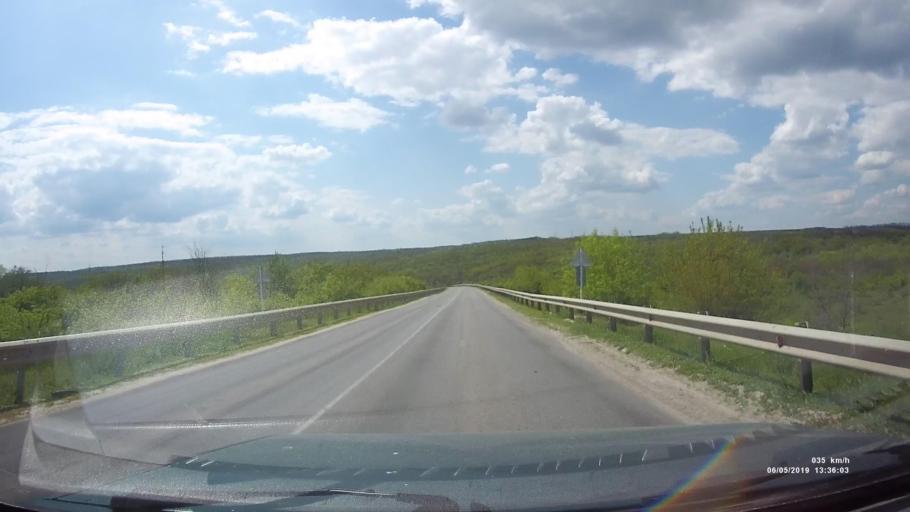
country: RU
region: Rostov
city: Ust'-Donetskiy
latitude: 47.6919
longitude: 40.7371
